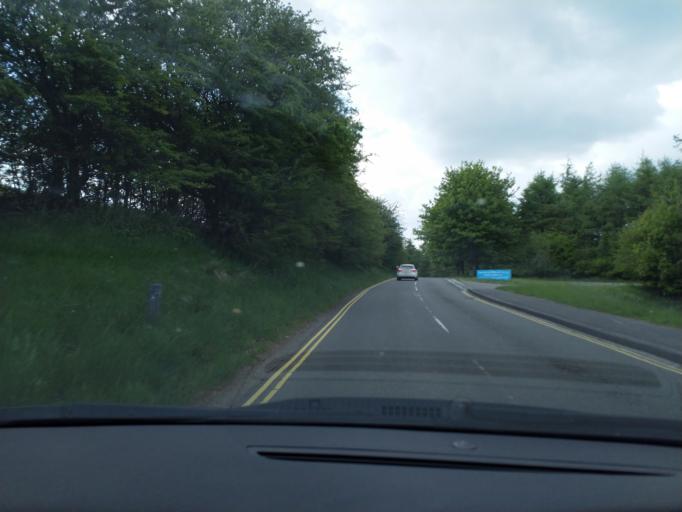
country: GB
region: England
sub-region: Derbyshire
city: Hope Valley
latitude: 53.3801
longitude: -1.7159
